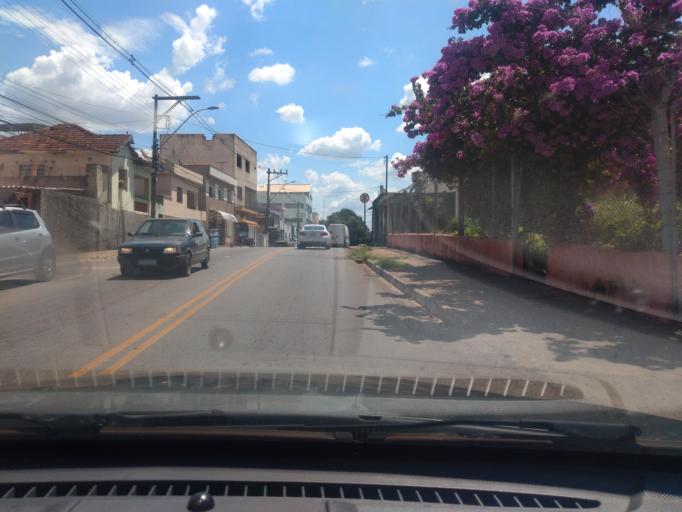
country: BR
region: Minas Gerais
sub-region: Tres Coracoes
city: Tres Coracoes
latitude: -21.6937
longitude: -45.2493
